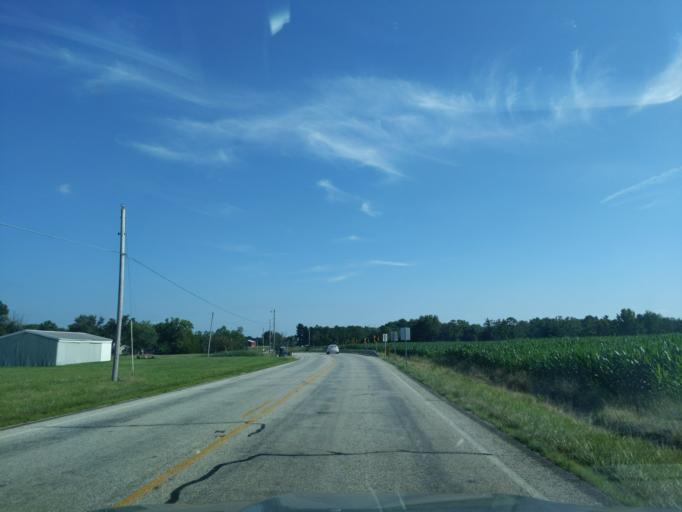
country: US
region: Indiana
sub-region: Ripley County
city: Osgood
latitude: 39.1058
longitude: -85.2792
